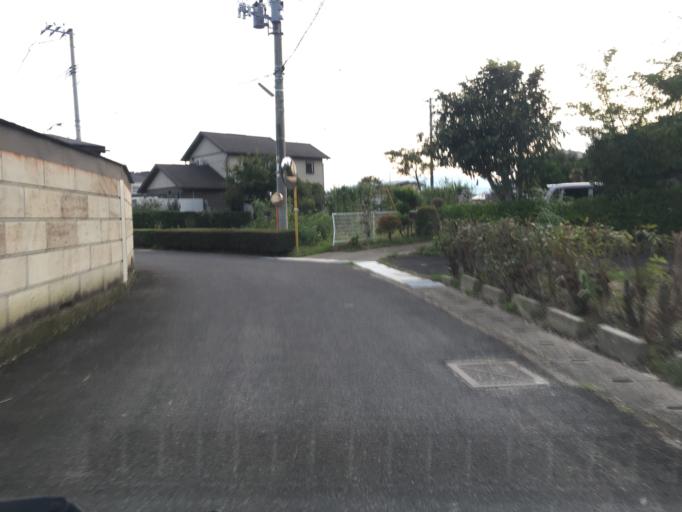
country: JP
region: Fukushima
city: Fukushima-shi
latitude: 37.7784
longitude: 140.5055
